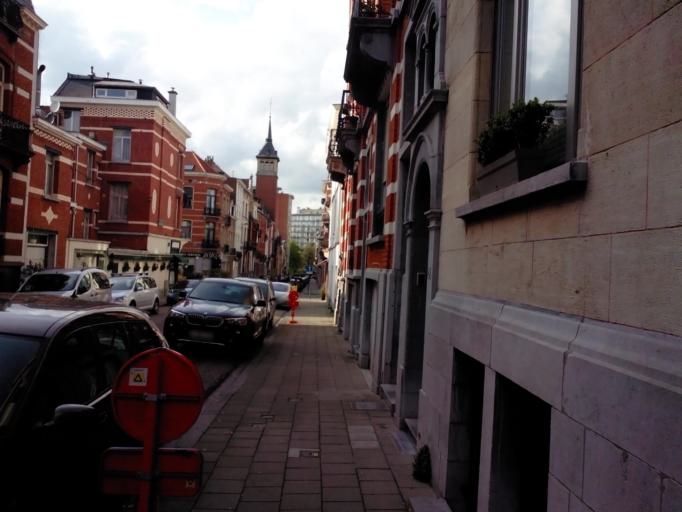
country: BE
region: Brussels Capital
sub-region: Bruxelles-Capitale
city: Brussels
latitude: 50.8450
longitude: 4.3876
